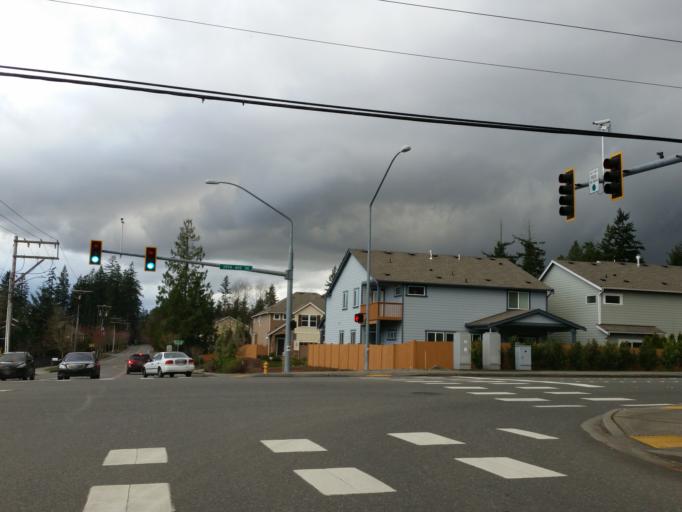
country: US
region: Washington
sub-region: Snohomish County
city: North Creek
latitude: 47.8055
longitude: -122.1806
